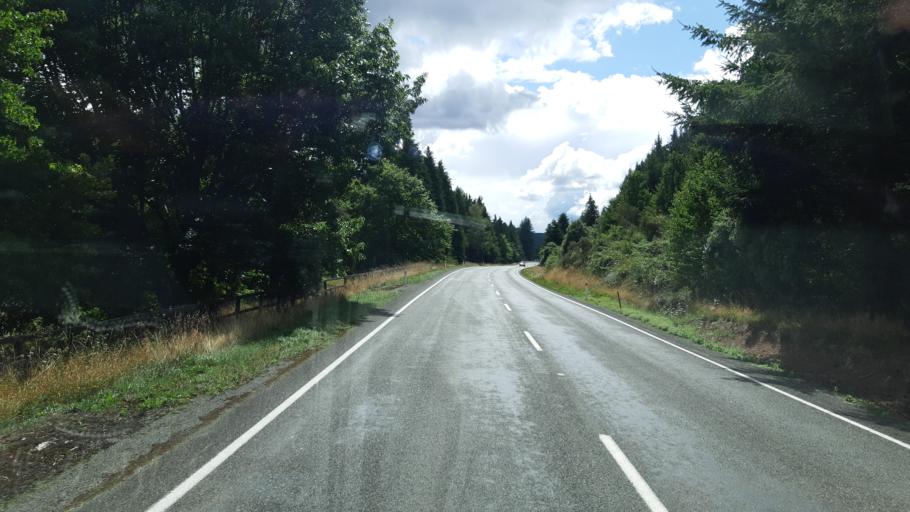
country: NZ
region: Tasman
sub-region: Tasman District
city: Wakefield
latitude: -41.5796
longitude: 172.7687
